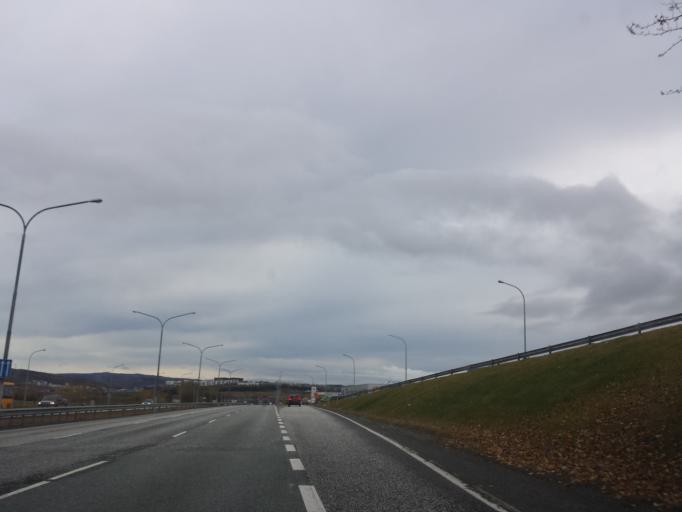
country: IS
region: Capital Region
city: Reykjavik
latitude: 64.1241
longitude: -21.8110
